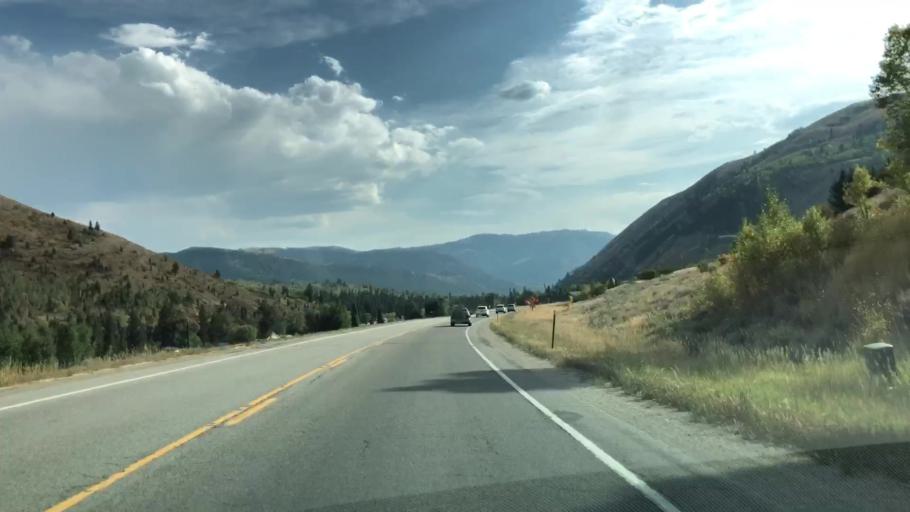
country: US
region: Wyoming
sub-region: Teton County
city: Hoback
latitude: 43.3510
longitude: -110.7202
